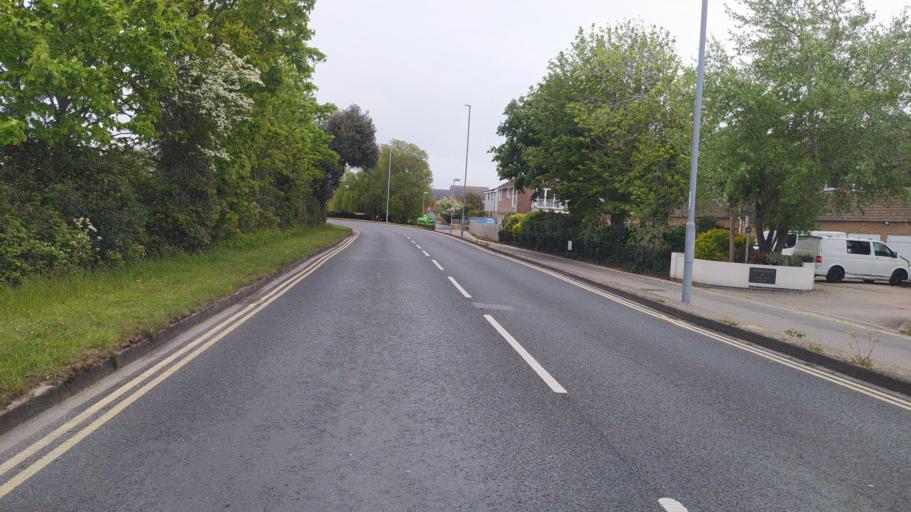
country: GB
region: England
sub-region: Dorset
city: Christchurch
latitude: 50.7312
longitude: -1.7848
